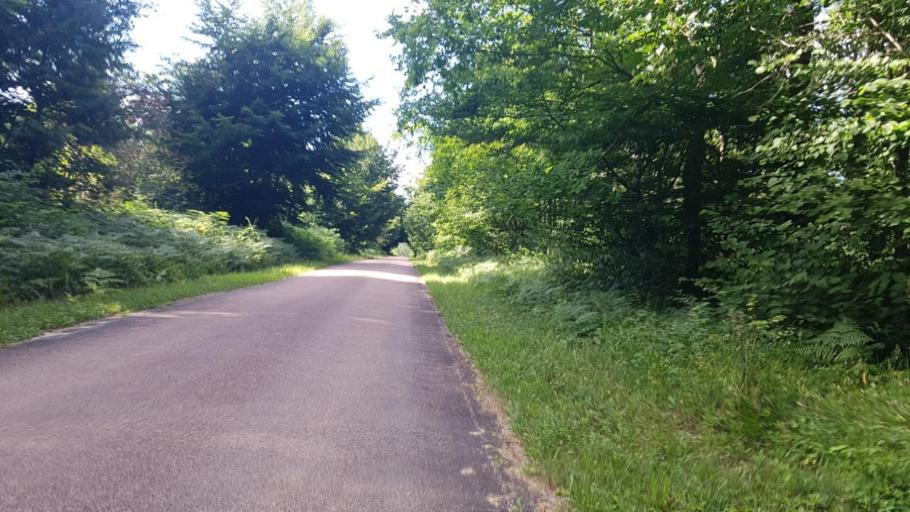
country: FR
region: Picardie
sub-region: Departement de l'Oise
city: Chamant
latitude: 49.1646
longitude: 2.6342
